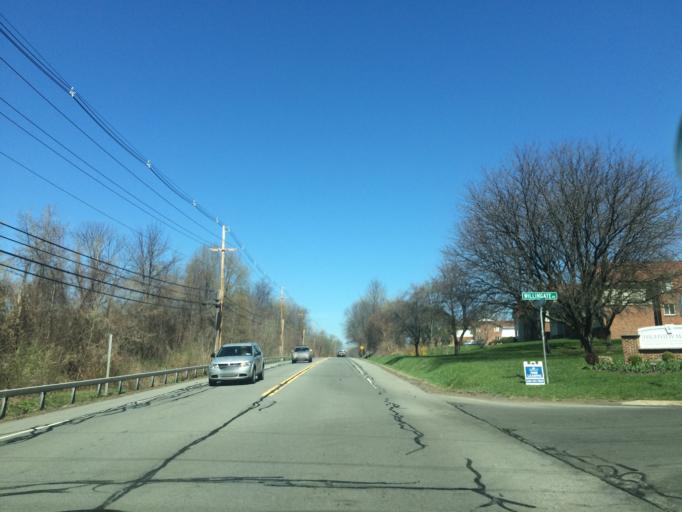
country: US
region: New York
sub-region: Monroe County
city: Fairport
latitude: 43.0972
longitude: -77.4260
